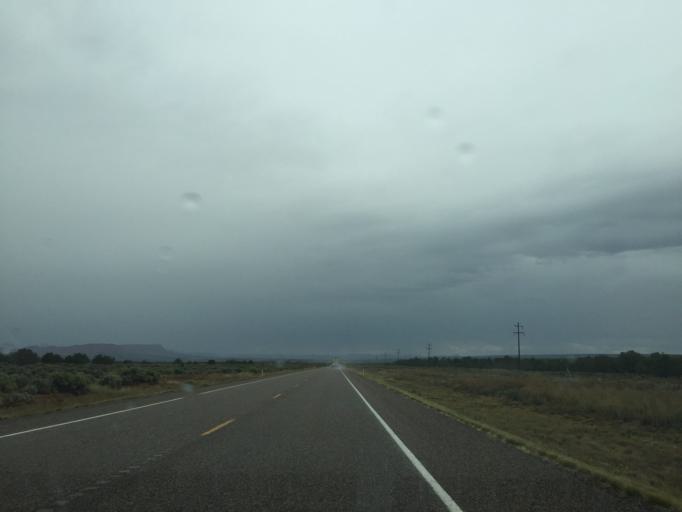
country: US
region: Utah
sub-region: Kane County
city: Kanab
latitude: 37.0854
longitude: -112.1541
